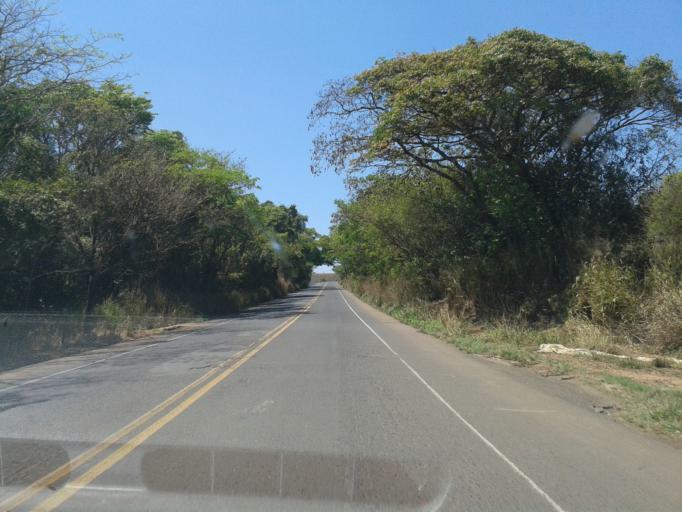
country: BR
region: Minas Gerais
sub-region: Araxa
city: Araxa
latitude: -19.4586
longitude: -47.1739
